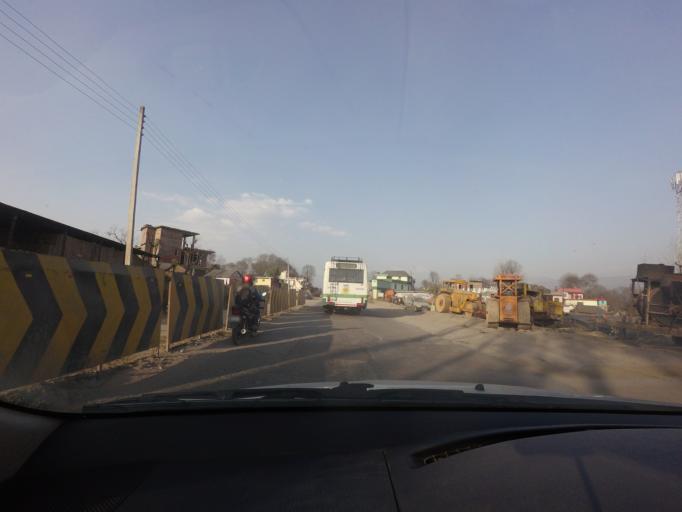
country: IN
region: Himachal Pradesh
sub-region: Mandi
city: Sundarnagar
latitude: 31.5610
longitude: 76.9034
